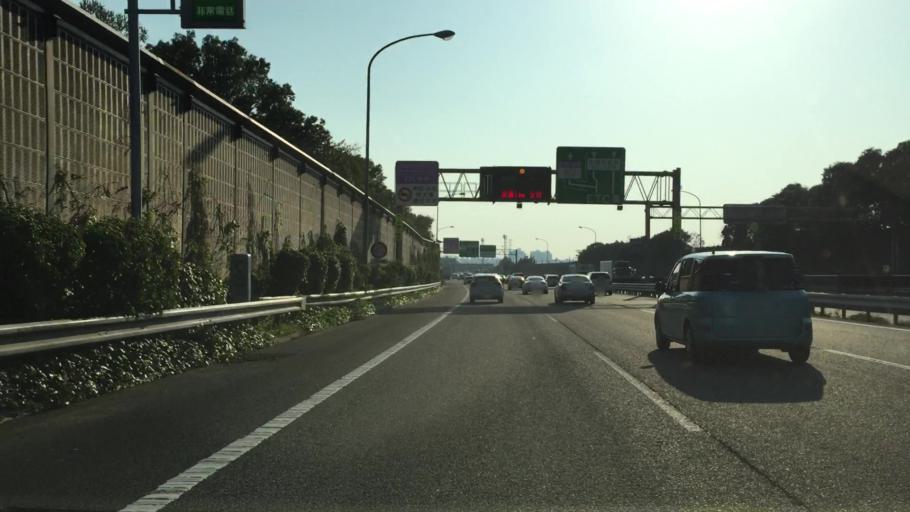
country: JP
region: Chiba
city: Nagareyama
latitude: 35.8703
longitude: 139.8869
